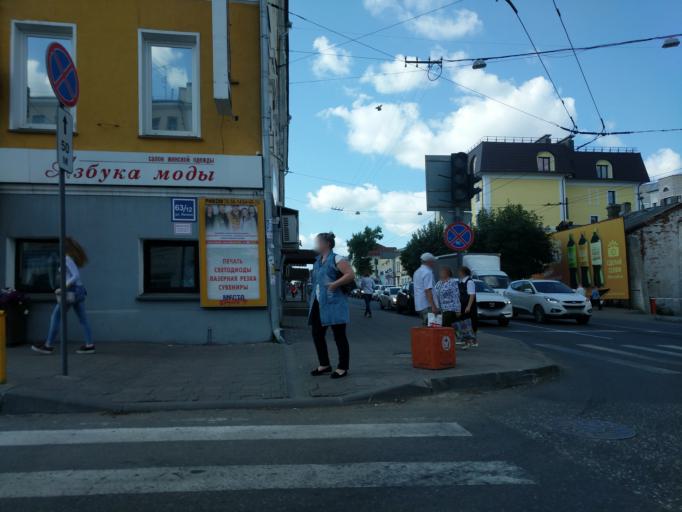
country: RU
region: Kirov
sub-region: Kirovo-Chepetskiy Rayon
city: Kirov
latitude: 58.6056
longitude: 49.6807
